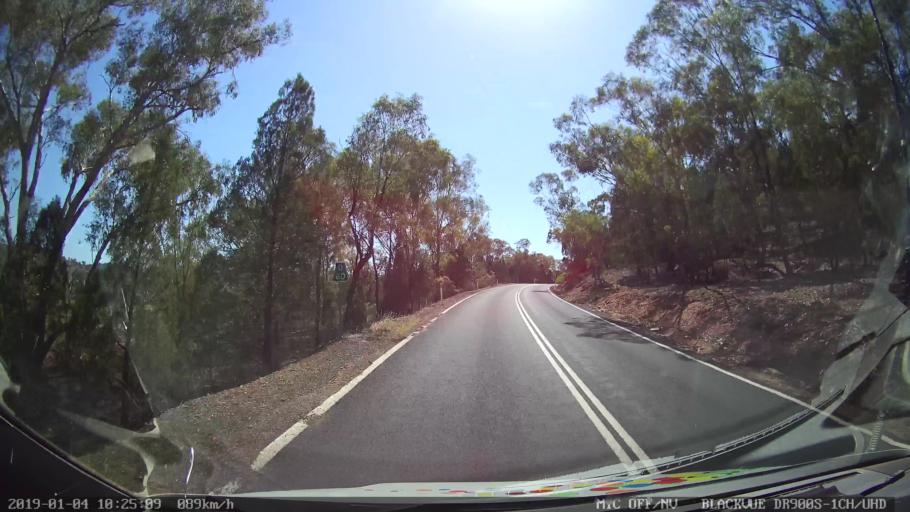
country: AU
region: New South Wales
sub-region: Cabonne
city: Canowindra
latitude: -33.3682
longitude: 148.5661
